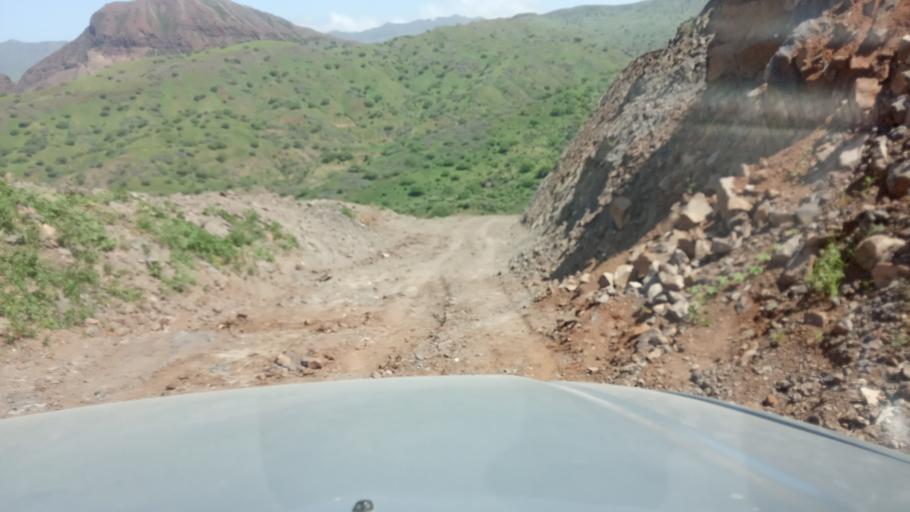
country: CV
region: Santa Catarina
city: Assomada
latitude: 15.1105
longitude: -23.7291
